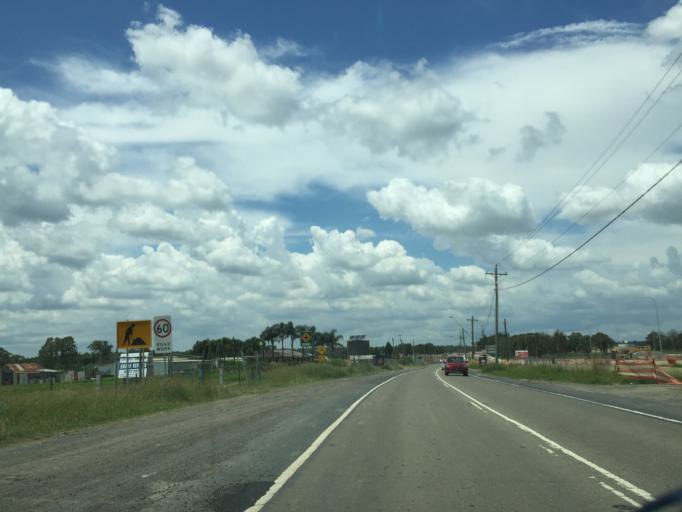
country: AU
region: New South Wales
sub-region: Blacktown
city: Hassall Grove
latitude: -33.7052
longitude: 150.8381
